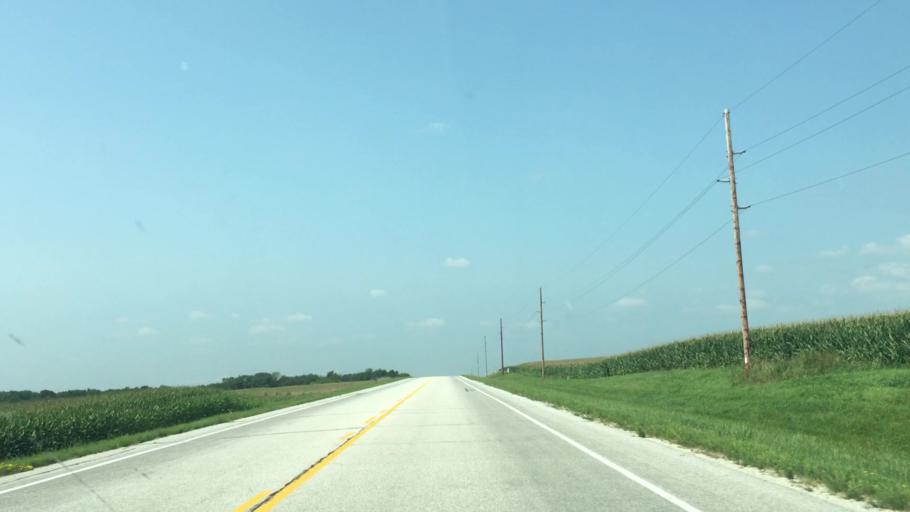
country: US
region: Minnesota
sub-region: Fillmore County
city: Harmony
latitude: 43.5681
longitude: -91.9296
